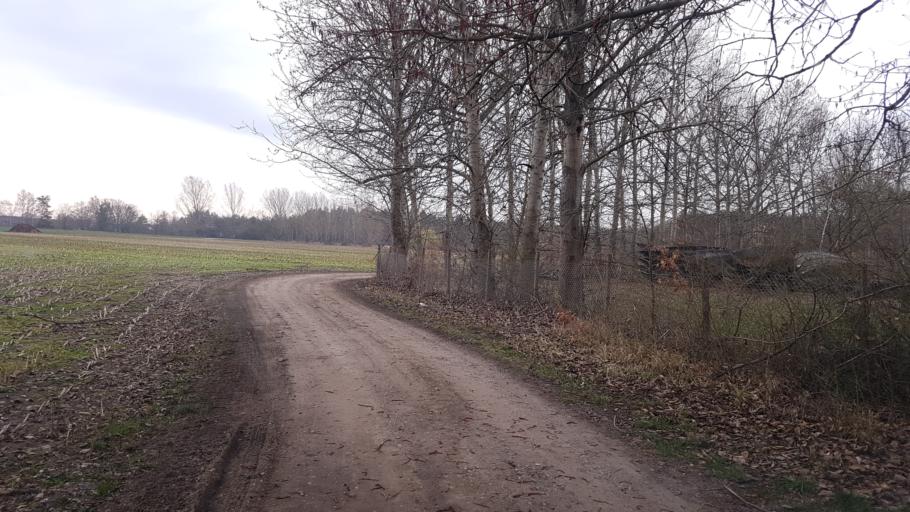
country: DE
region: Brandenburg
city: Doberlug-Kirchhain
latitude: 51.6590
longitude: 13.5176
